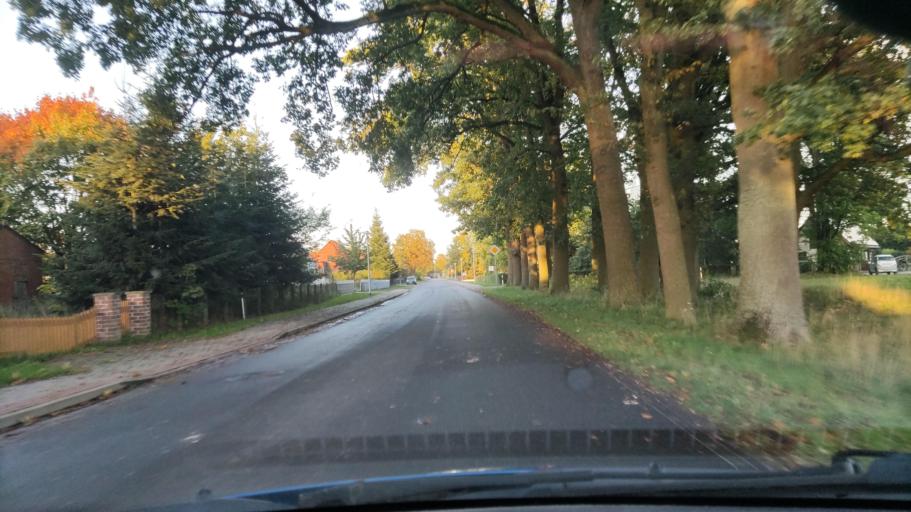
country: DE
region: Mecklenburg-Vorpommern
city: Lubtheen
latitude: 53.3145
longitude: 11.0063
